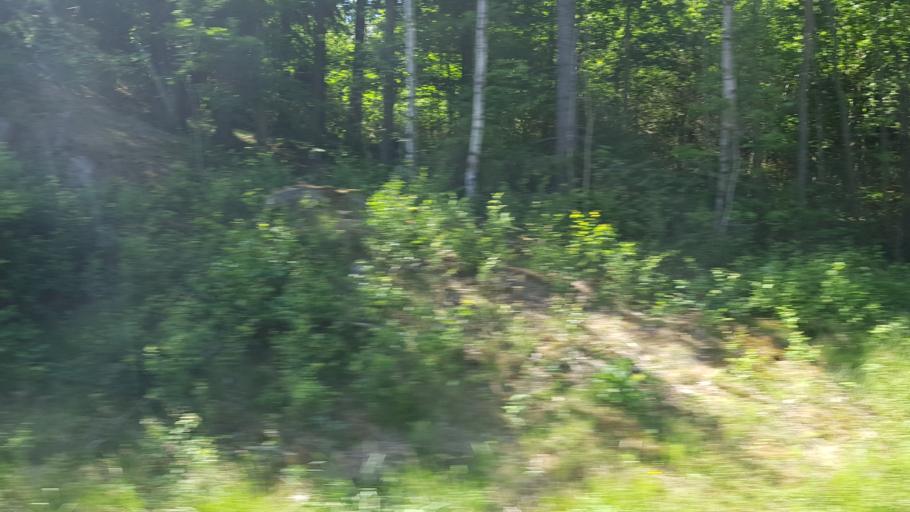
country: SE
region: Vaestra Goetaland
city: Ronnang
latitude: 57.9903
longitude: 11.6577
